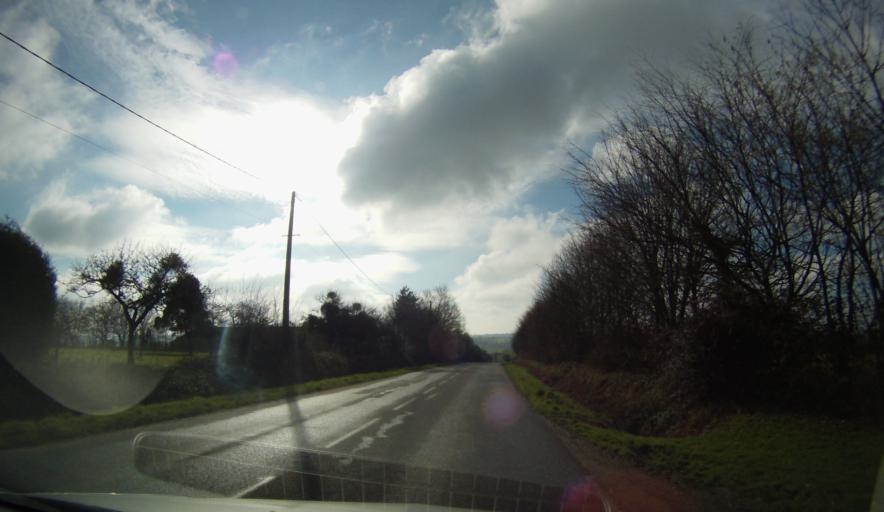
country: FR
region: Brittany
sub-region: Departement d'Ille-et-Vilaine
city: Corps-Nuds
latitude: 47.9572
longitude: -1.5681
